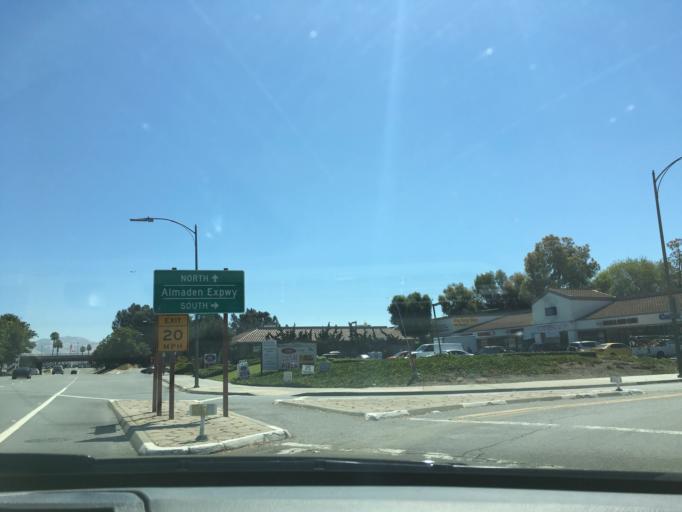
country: US
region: California
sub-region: Santa Clara County
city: Seven Trees
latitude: 37.2745
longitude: -121.8815
